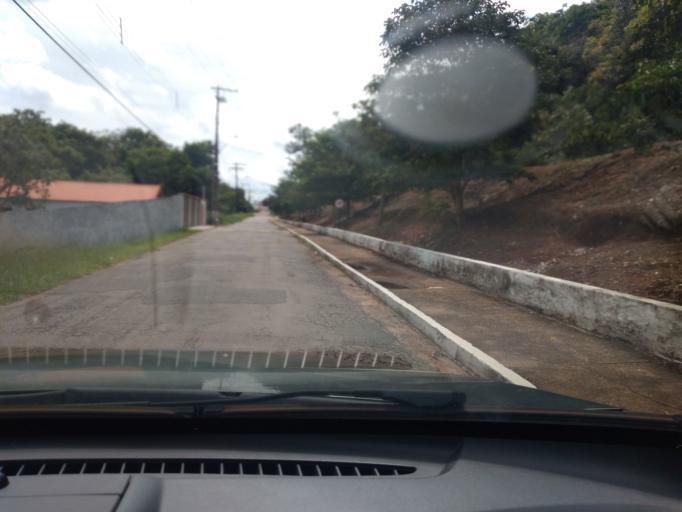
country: BR
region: Minas Gerais
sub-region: Tres Coracoes
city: Tres Coracoes
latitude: -21.7003
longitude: -45.2696
